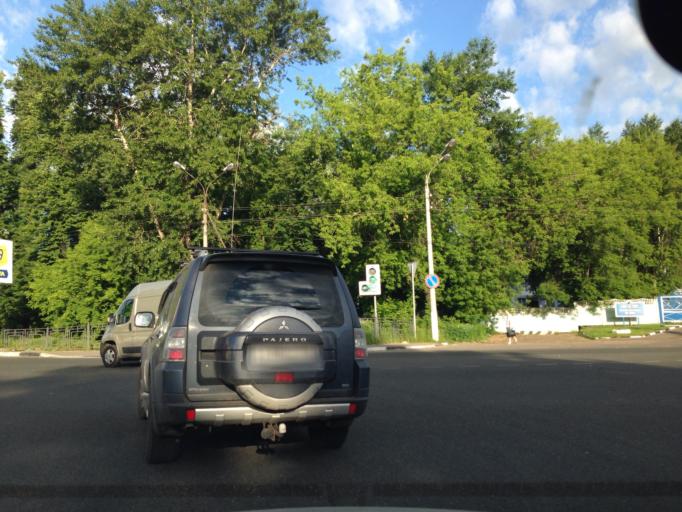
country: RU
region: Moskovskaya
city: Balashikha
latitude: 55.8142
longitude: 37.9550
